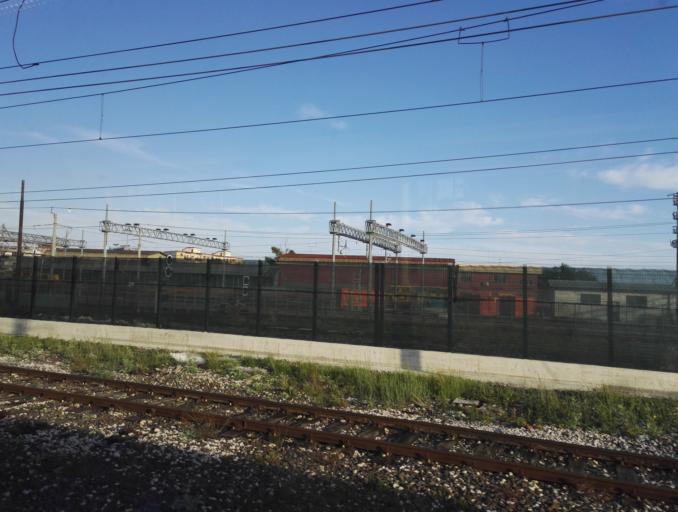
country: IT
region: Campania
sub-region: Provincia di Napoli
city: Napoli
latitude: 40.8533
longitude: 14.2807
